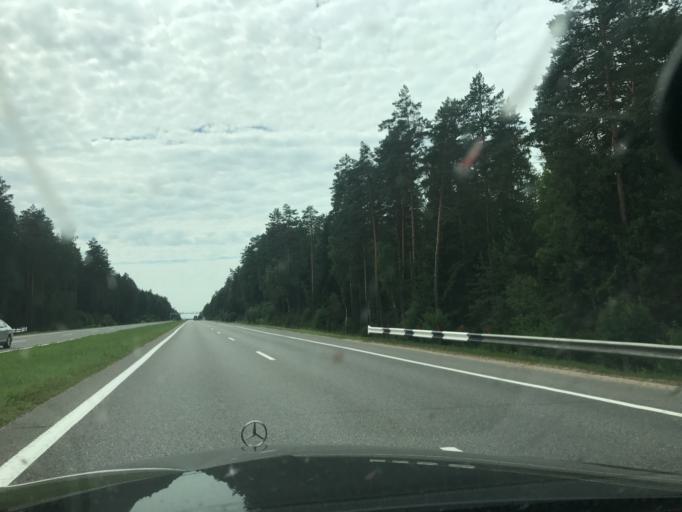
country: BY
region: Minsk
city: Slabada
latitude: 53.9076
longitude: 27.9490
